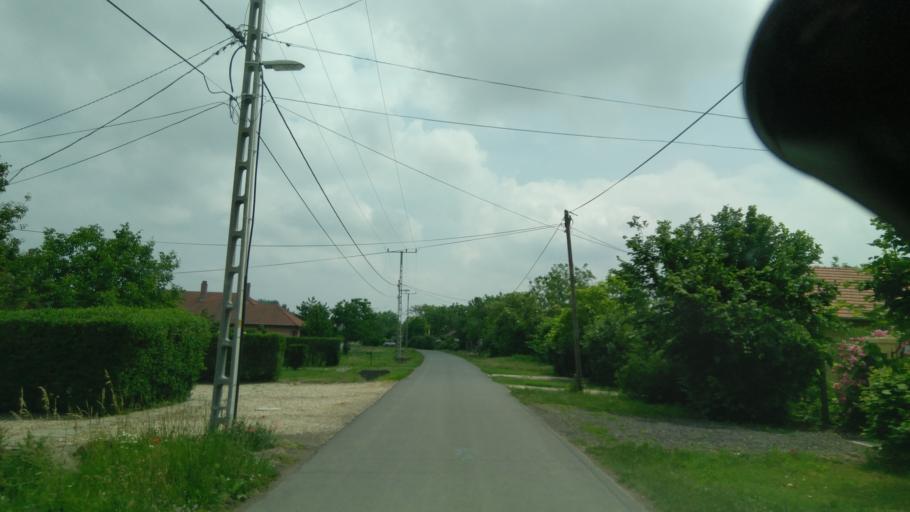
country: HU
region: Bekes
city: Gyula
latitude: 46.6588
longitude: 21.2525
